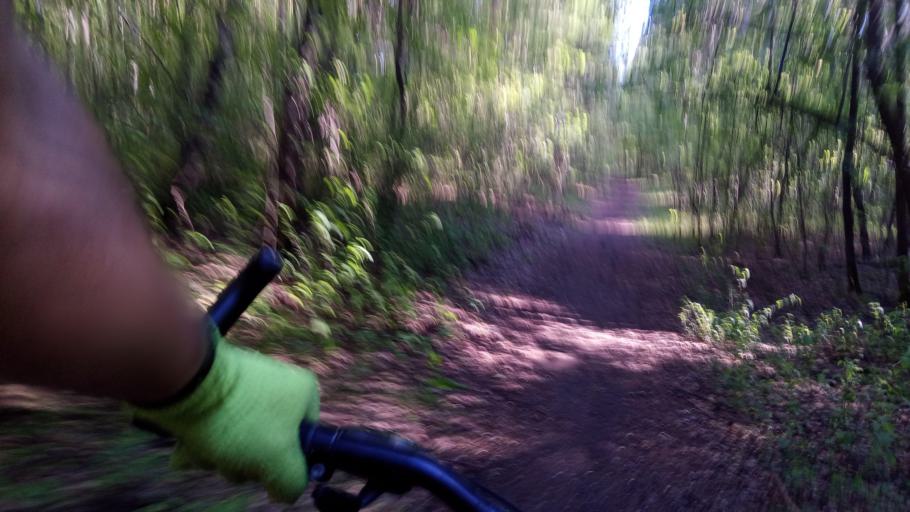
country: RU
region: Chelyabinsk
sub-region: Gorod Chelyabinsk
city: Chelyabinsk
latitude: 55.1504
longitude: 61.3471
